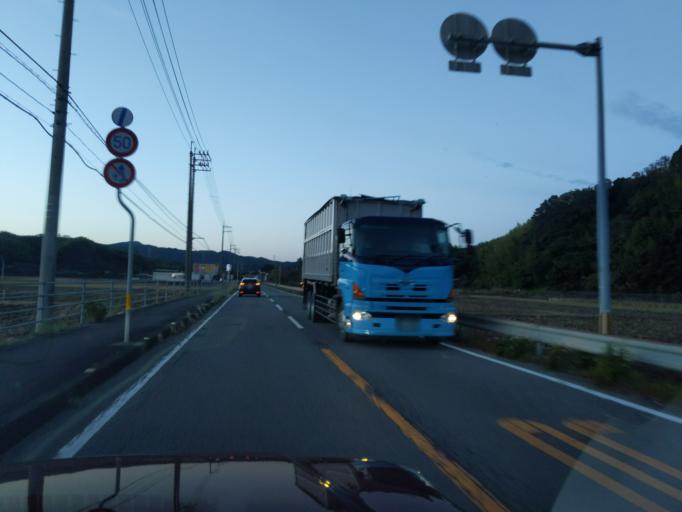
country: JP
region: Tokushima
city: Anan
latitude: 33.8541
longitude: 134.6270
